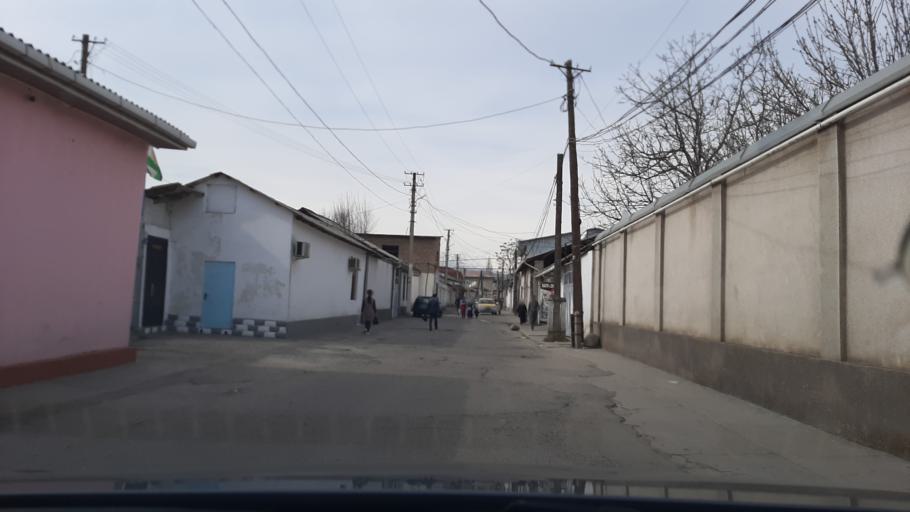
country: TJ
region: Dushanbe
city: Dushanbe
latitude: 38.5626
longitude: 68.7750
